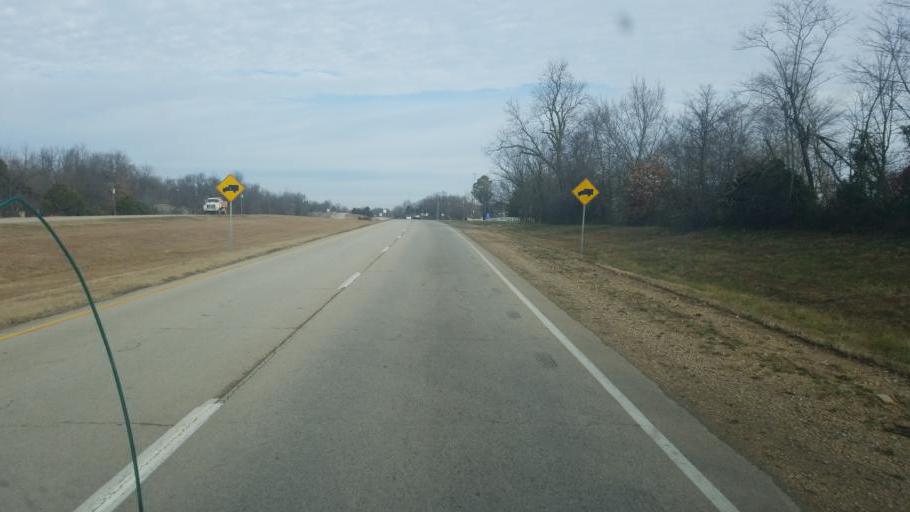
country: US
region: Missouri
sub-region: Stoddard County
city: Dexter
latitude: 36.8313
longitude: -89.9412
